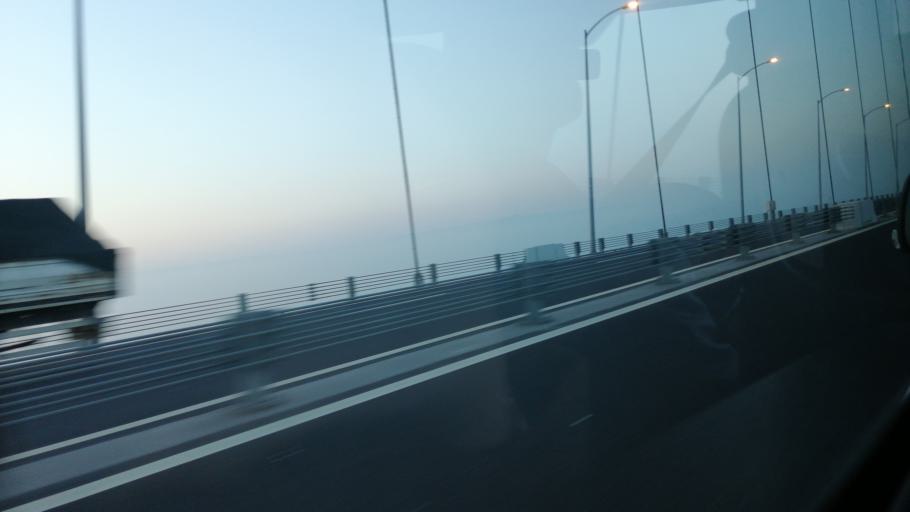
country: TR
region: Kocaeli
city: Tavsancil
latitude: 40.7586
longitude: 29.5164
